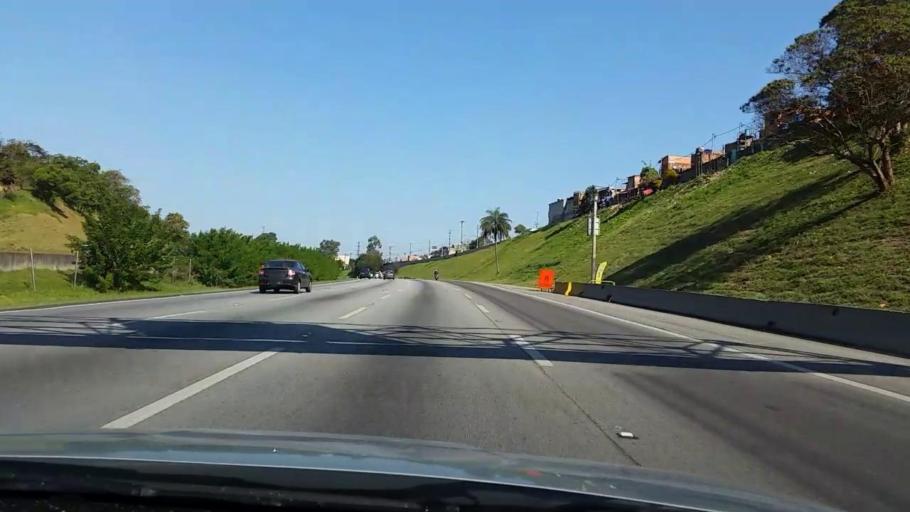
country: BR
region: Sao Paulo
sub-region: Diadema
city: Diadema
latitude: -23.6677
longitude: -46.6329
